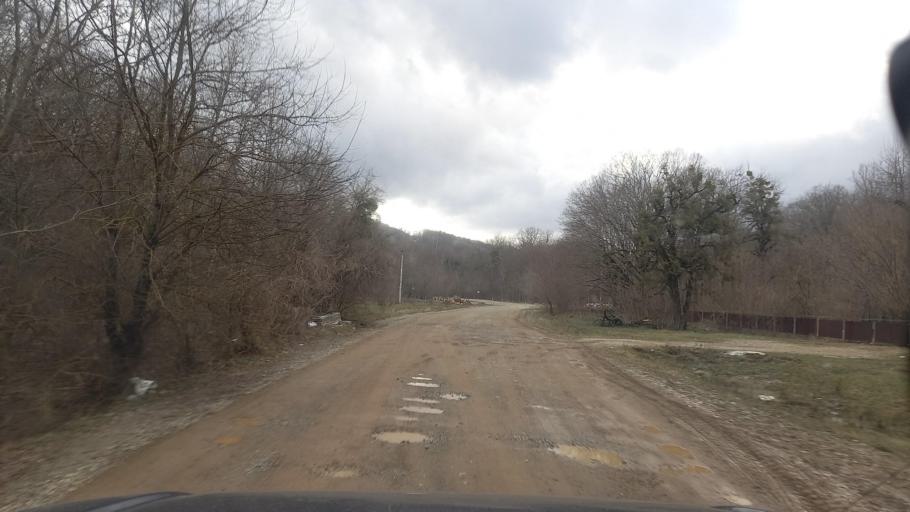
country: RU
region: Krasnodarskiy
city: Smolenskaya
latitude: 44.5606
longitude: 38.7972
